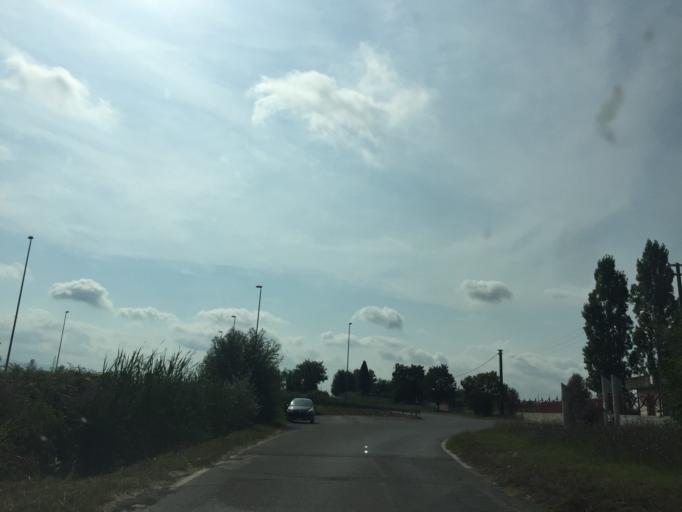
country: IT
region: Tuscany
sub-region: Provincia di Pistoia
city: Cintolese
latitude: 43.8391
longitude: 10.8205
